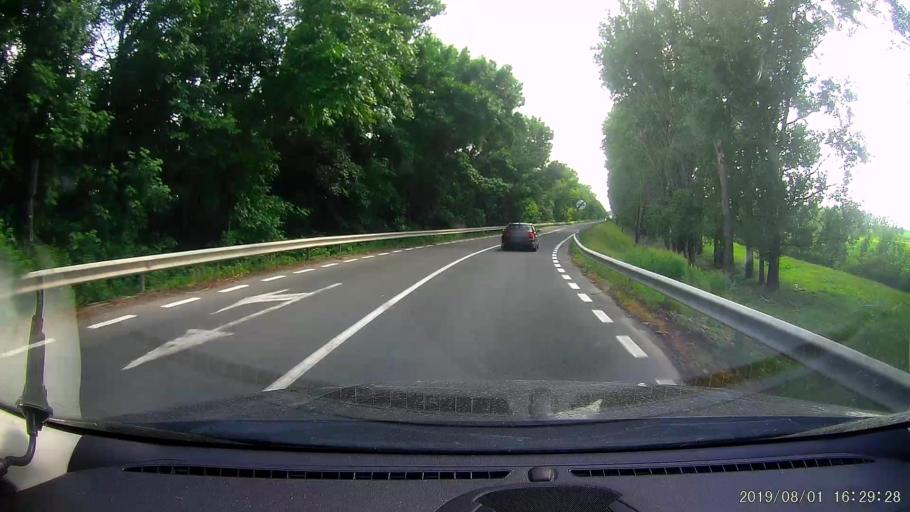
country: BG
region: Silistra
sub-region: Obshtina Silistra
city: Silistra
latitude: 44.1407
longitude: 27.2894
